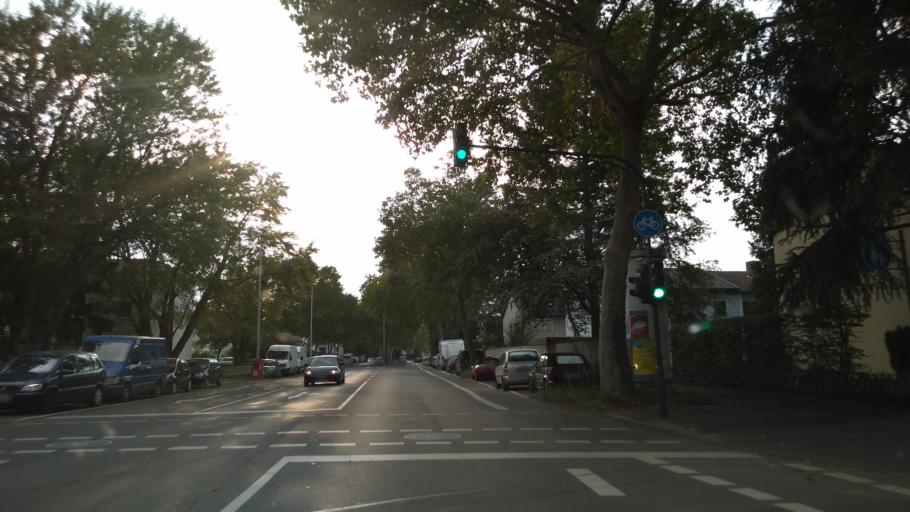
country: DE
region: North Rhine-Westphalia
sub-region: Regierungsbezirk Koln
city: Alfter
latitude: 50.7398
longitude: 7.0508
